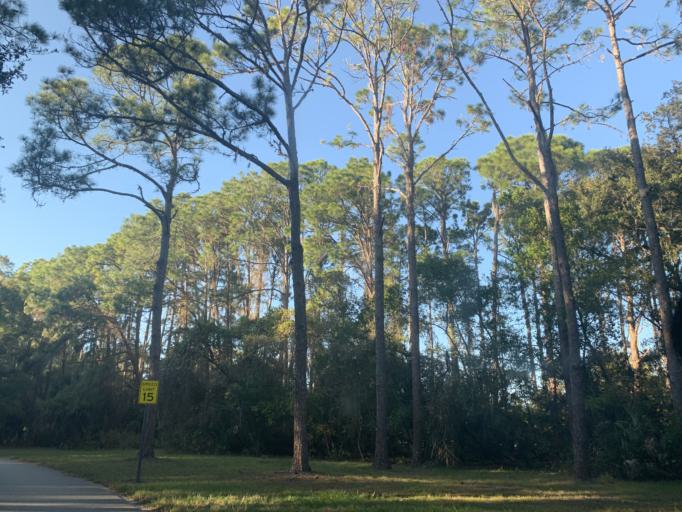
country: US
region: Florida
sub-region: Pinellas County
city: East Lake
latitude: 28.0911
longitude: -82.7039
